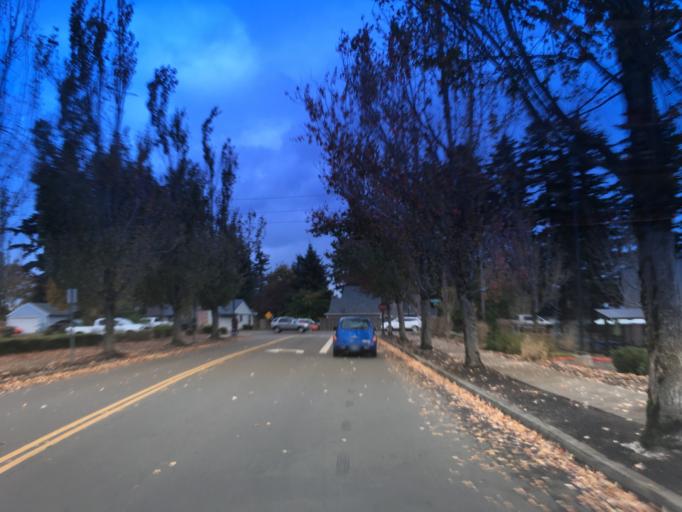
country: US
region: Oregon
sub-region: Multnomah County
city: Fairview
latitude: 45.5332
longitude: -122.4420
